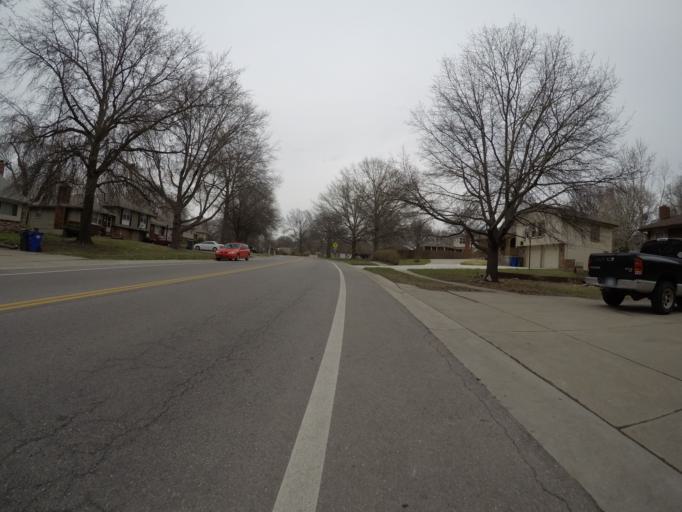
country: US
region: Kansas
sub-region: Johnson County
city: Olathe
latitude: 38.8698
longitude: -94.7922
